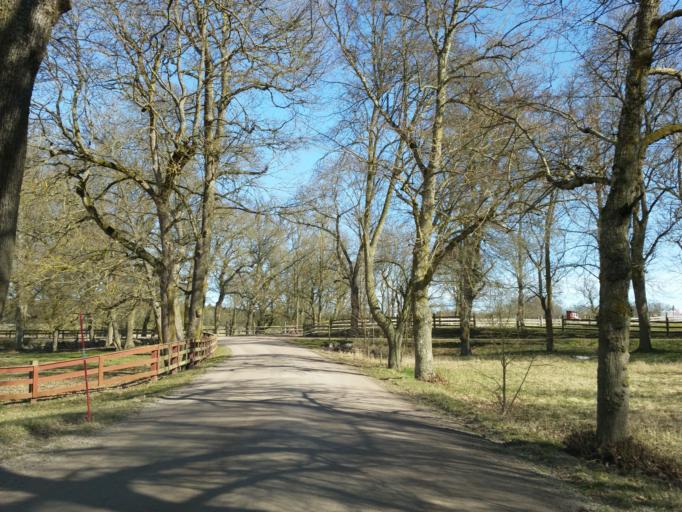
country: SE
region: Kalmar
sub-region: Monsteras Kommun
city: Timmernabben
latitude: 56.9367
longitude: 16.4234
